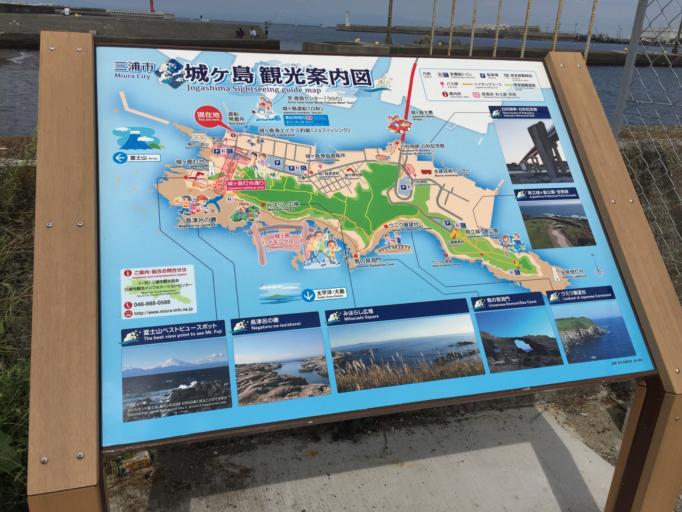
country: JP
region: Kanagawa
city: Miura
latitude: 35.1373
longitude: 139.6129
